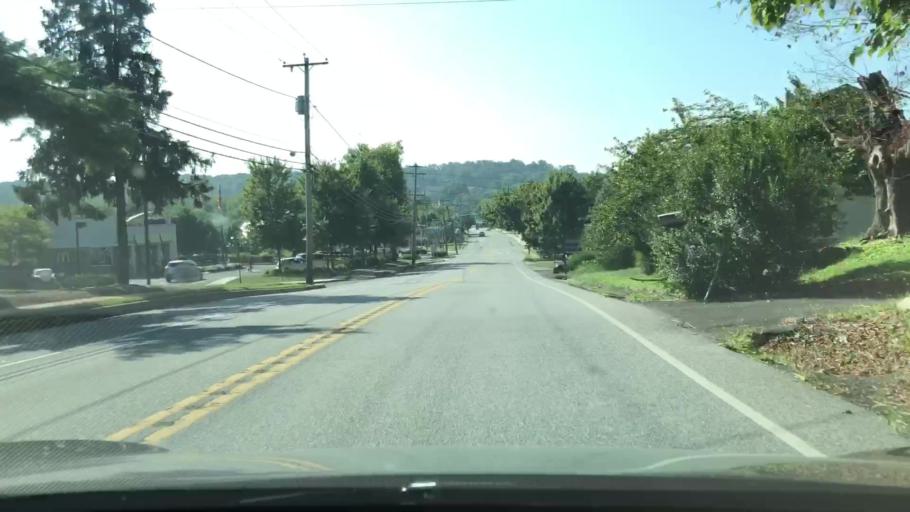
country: US
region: Pennsylvania
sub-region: Montgomery County
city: Dresher
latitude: 40.1447
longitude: -75.1685
